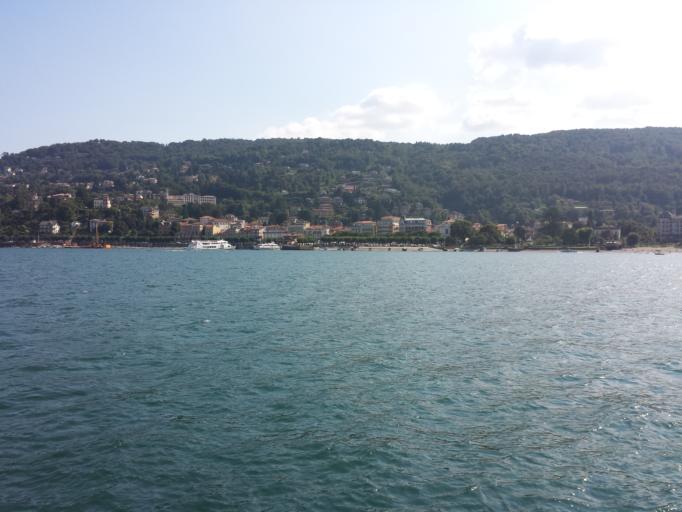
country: IT
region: Piedmont
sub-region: Provincia Verbano-Cusio-Ossola
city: Stresa
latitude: 45.8895
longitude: 8.5414
